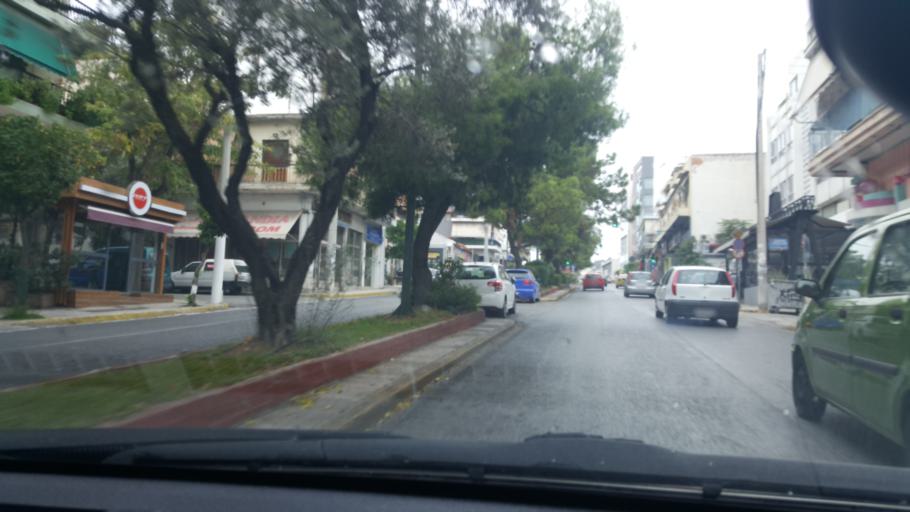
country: GR
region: Attica
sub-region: Nomarchia Athinas
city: Neo Psychiko
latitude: 37.9952
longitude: 23.7733
